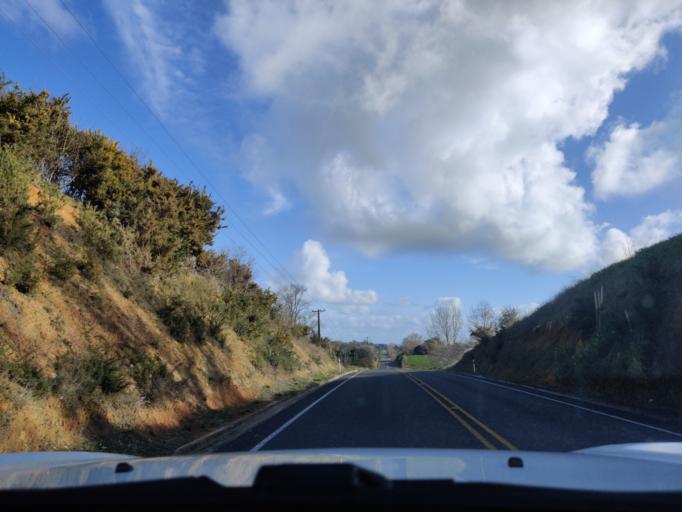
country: NZ
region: Waikato
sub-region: Waikato District
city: Te Kauwhata
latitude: -37.3703
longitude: 175.2406
